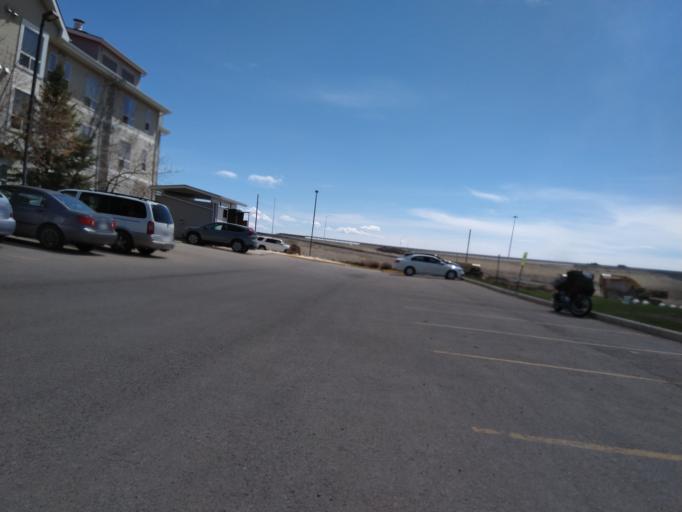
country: CA
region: Alberta
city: Calgary
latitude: 51.0100
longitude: -114.1598
